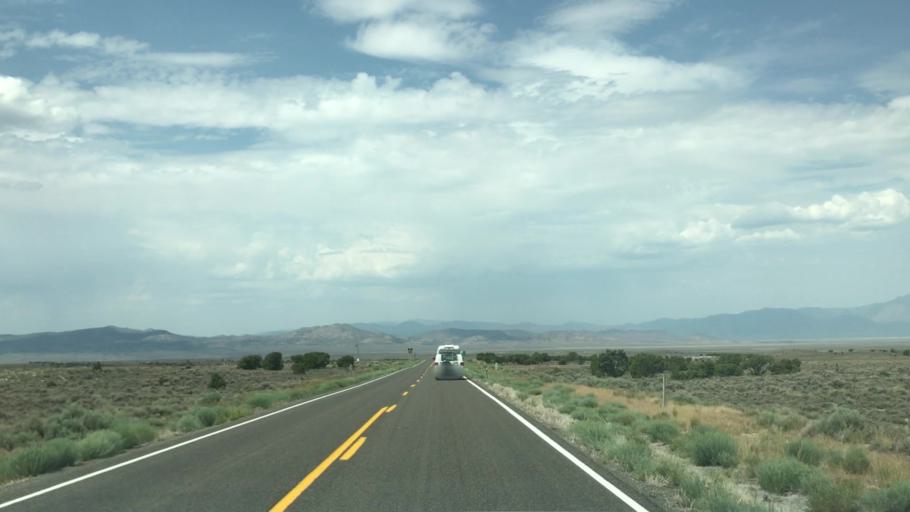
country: US
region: Nevada
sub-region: Eureka County
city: Eureka
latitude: 39.3937
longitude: -115.5211
